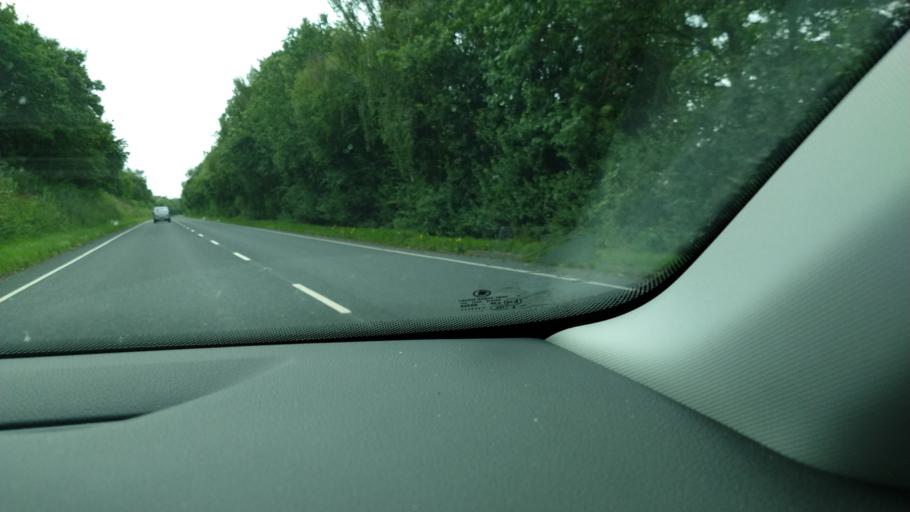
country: GB
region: England
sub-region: East Riding of Yorkshire
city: Barmby on the Marsh
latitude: 53.7218
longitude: -0.9792
